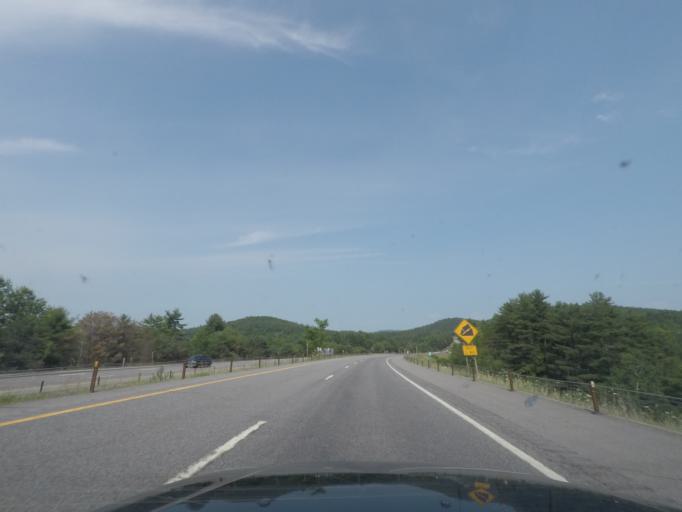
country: US
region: New York
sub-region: Essex County
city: Elizabethtown
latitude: 44.1957
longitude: -73.5352
